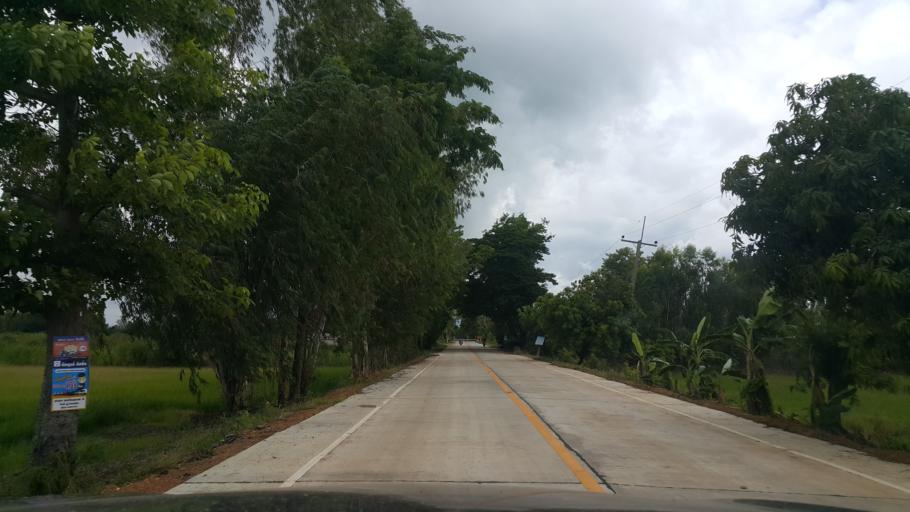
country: TH
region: Sukhothai
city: Kong Krailat
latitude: 16.9270
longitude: 99.9023
